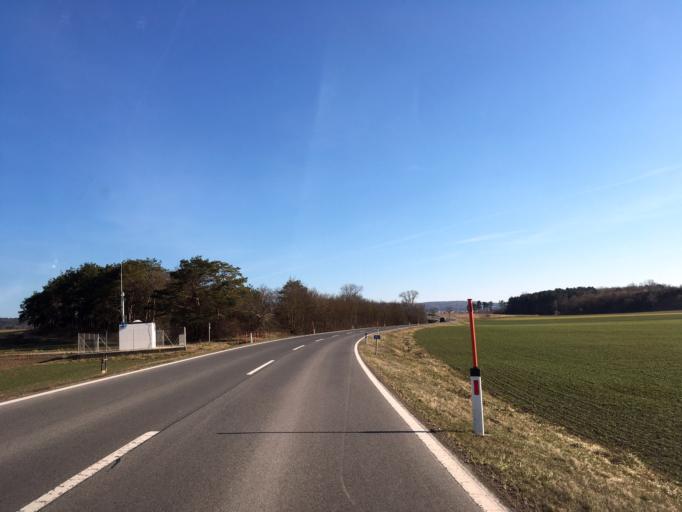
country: AT
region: Burgenland
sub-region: Eisenstadt-Umgebung
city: Wimpassing an der Leitha
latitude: 47.9095
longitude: 16.4318
